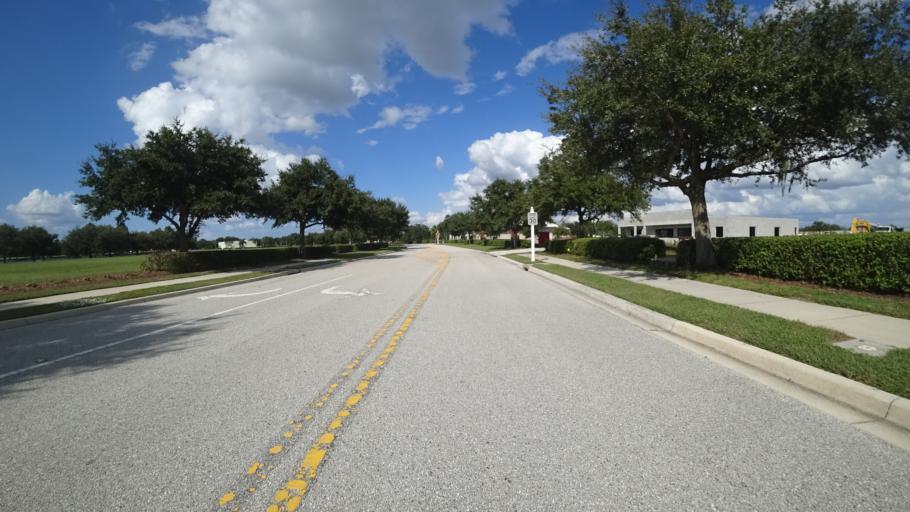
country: US
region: Florida
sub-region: Sarasota County
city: Desoto Lakes
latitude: 27.4590
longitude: -82.4369
